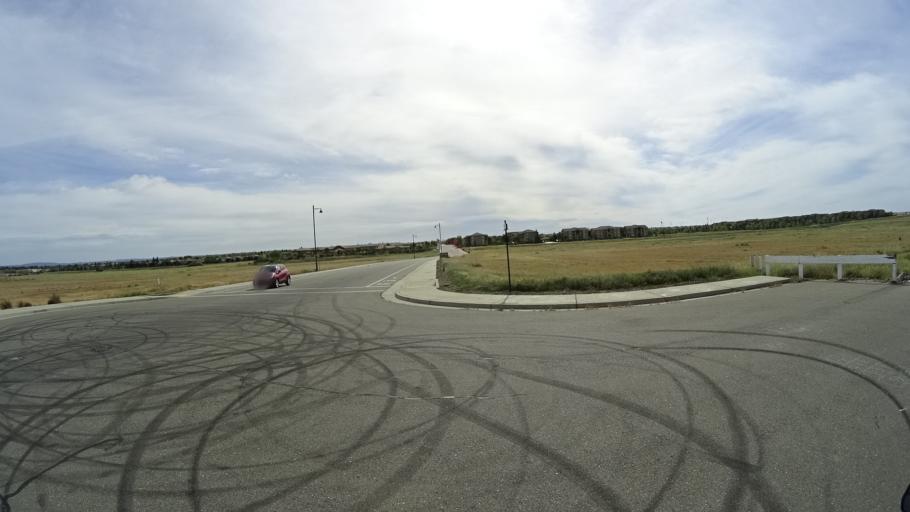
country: US
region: California
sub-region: Placer County
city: Lincoln
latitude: 38.8375
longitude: -121.2971
